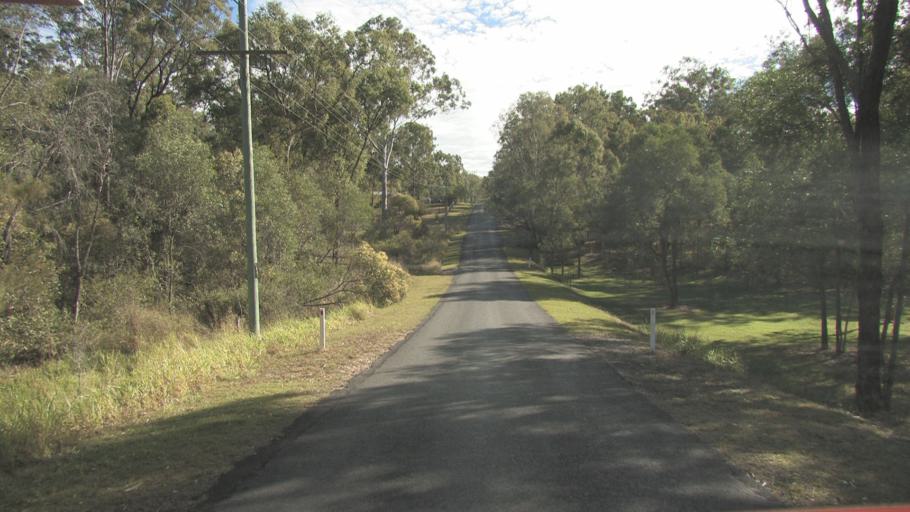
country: AU
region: Queensland
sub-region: Logan
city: Cedar Vale
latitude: -27.8362
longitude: 153.0683
